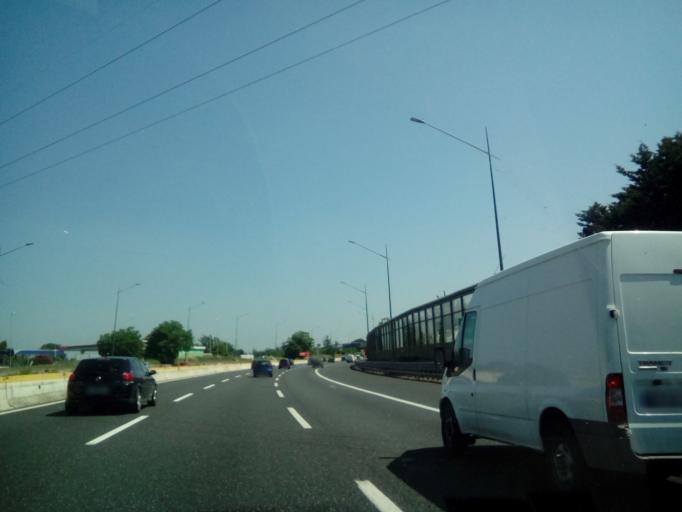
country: IT
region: Latium
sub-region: Citta metropolitana di Roma Capitale
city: Valle Santa
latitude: 41.9561
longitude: 12.3846
